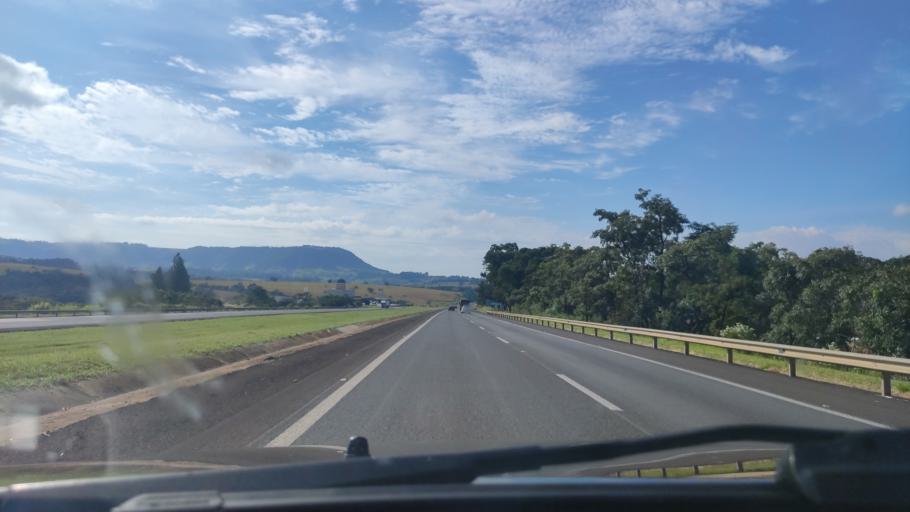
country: BR
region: Sao Paulo
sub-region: Itatinga
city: Itatinga
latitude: -23.1455
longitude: -48.4078
